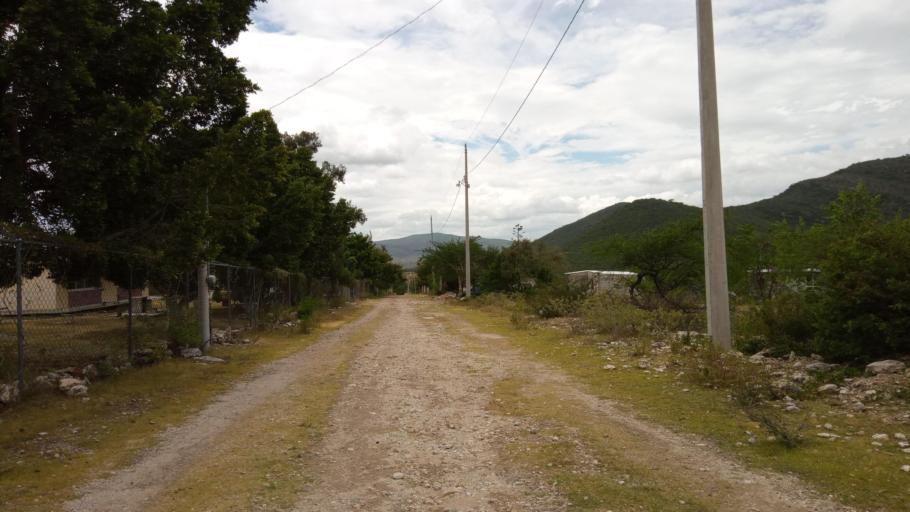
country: MX
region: Puebla
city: Totoltepec de Guerrero
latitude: 18.2956
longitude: -97.7731
